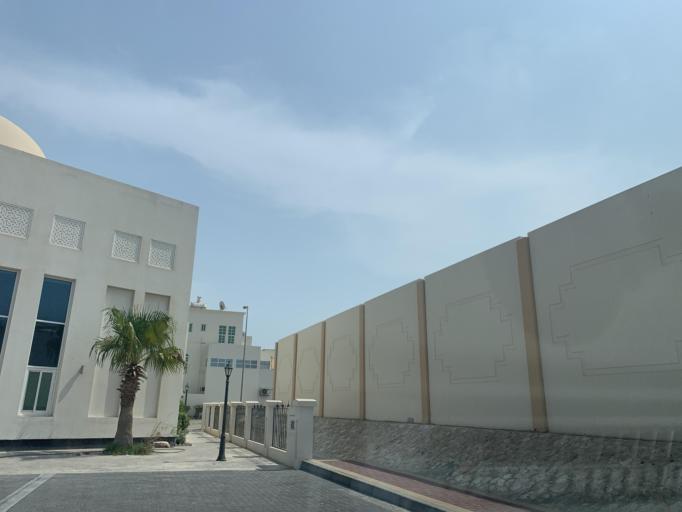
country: BH
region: Muharraq
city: Al Hadd
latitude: 26.2677
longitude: 50.6586
